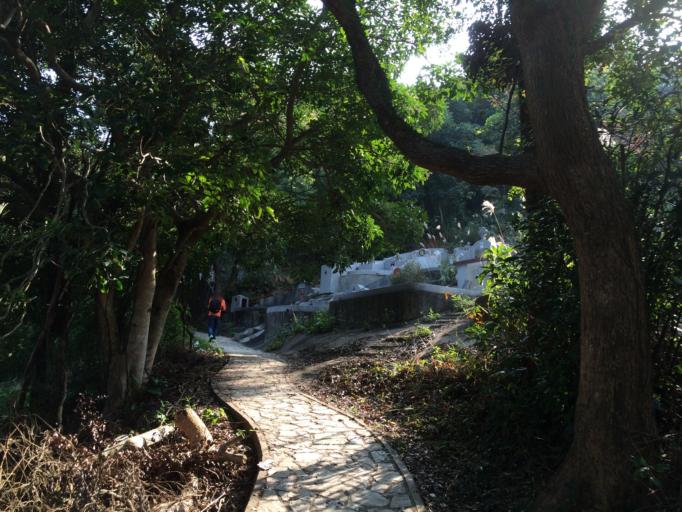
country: HK
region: Tai Po
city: Tai Po
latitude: 22.4523
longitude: 114.2141
